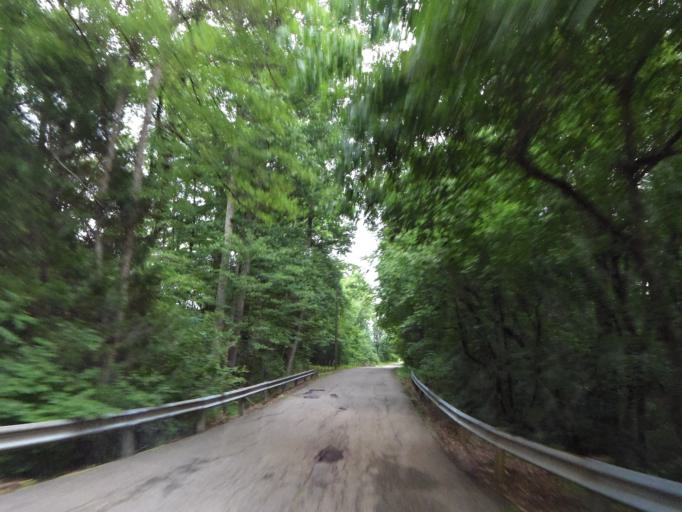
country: US
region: Tennessee
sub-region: Sevier County
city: Seymour
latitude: 35.9464
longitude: -83.7988
